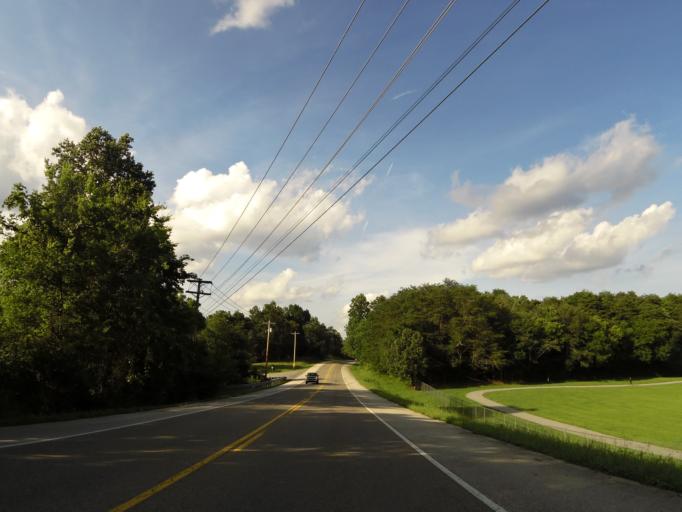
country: US
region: Tennessee
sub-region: Blount County
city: Louisville
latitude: 35.8382
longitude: -84.0075
